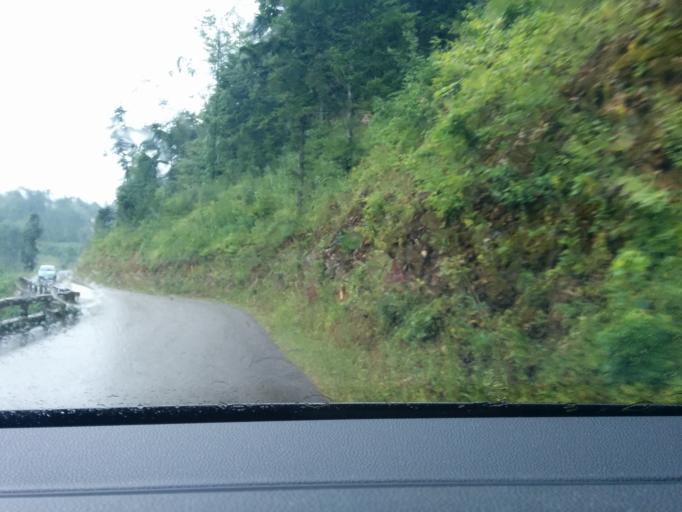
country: FR
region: Franche-Comte
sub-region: Departement du Jura
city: Valfin-les-Saint-Claude
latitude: 46.4683
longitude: 5.8369
